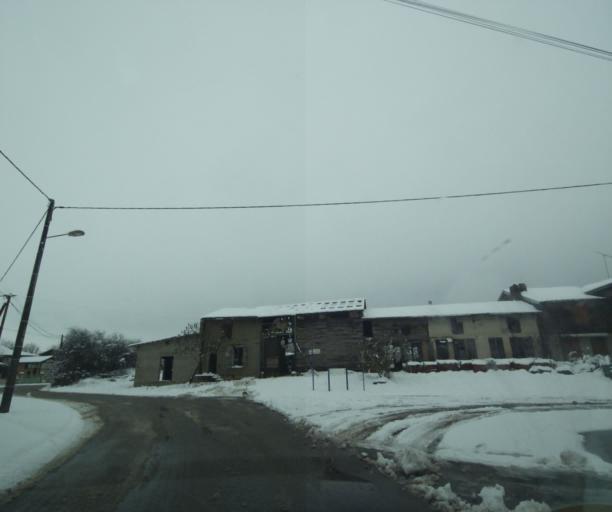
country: FR
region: Champagne-Ardenne
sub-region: Departement de la Haute-Marne
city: Montier-en-Der
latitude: 48.5080
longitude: 4.7839
